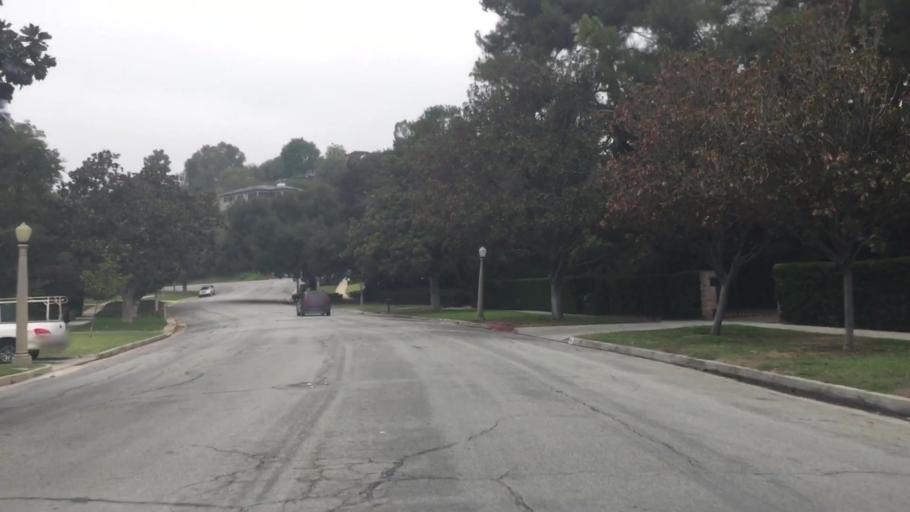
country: US
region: California
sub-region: Los Angeles County
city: San Marino
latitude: 34.1196
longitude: -118.1249
